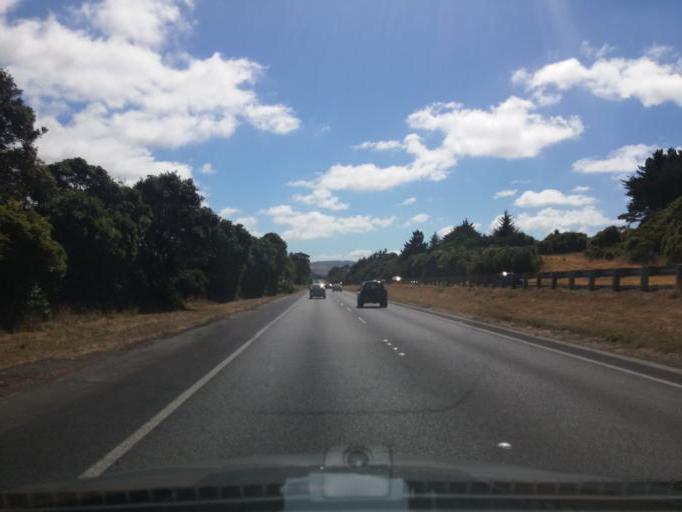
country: NZ
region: Wellington
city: Petone
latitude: -41.2165
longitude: 174.8120
